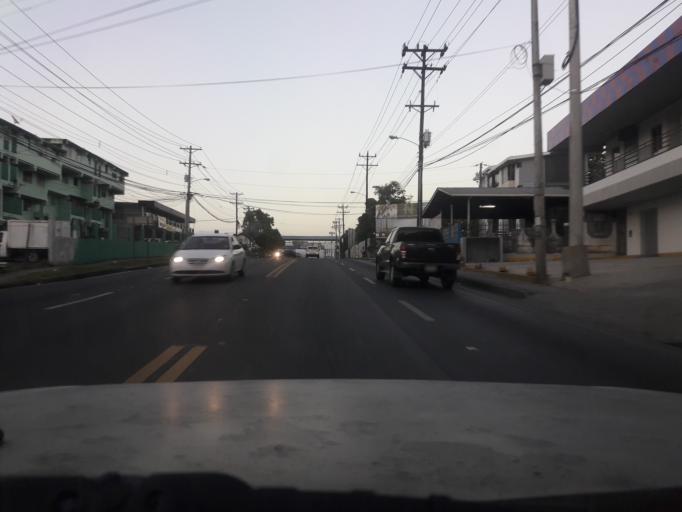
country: PA
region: Panama
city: San Miguelito
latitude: 9.0522
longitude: -79.4357
